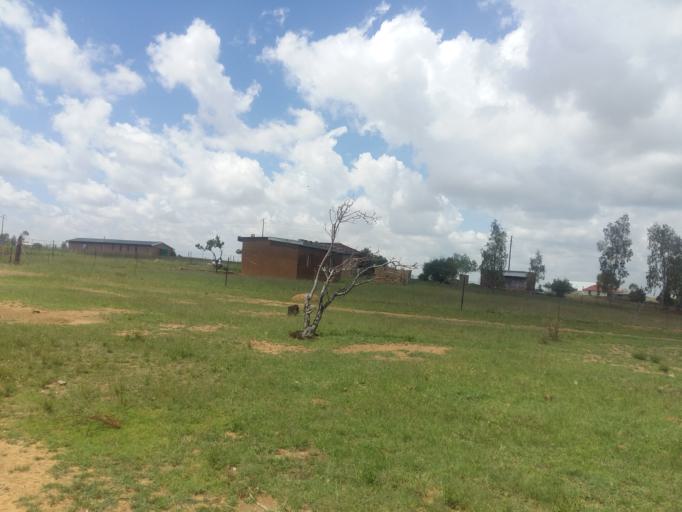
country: LS
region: Mafeteng
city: Mafeteng
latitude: -29.7534
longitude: 27.1148
